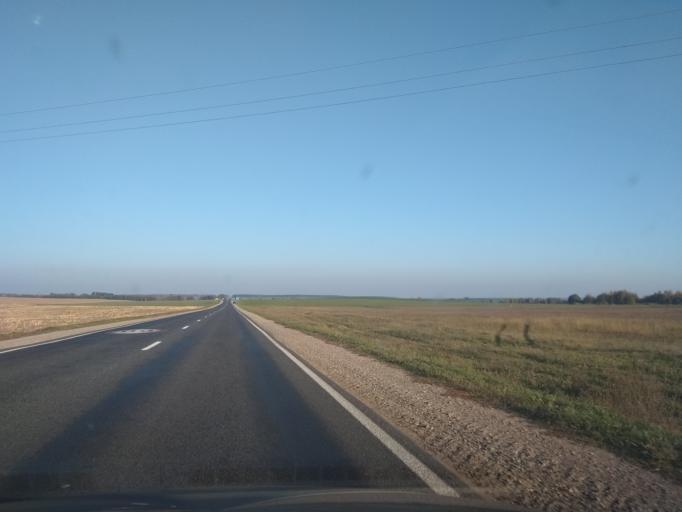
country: BY
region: Grodnenskaya
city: Svislach
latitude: 53.1323
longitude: 24.2031
